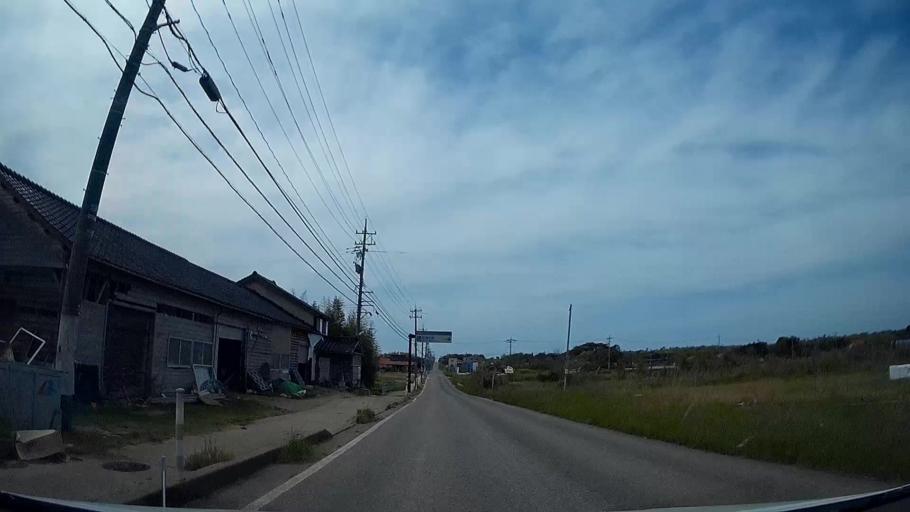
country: JP
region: Ishikawa
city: Hakui
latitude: 37.0122
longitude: 136.7594
